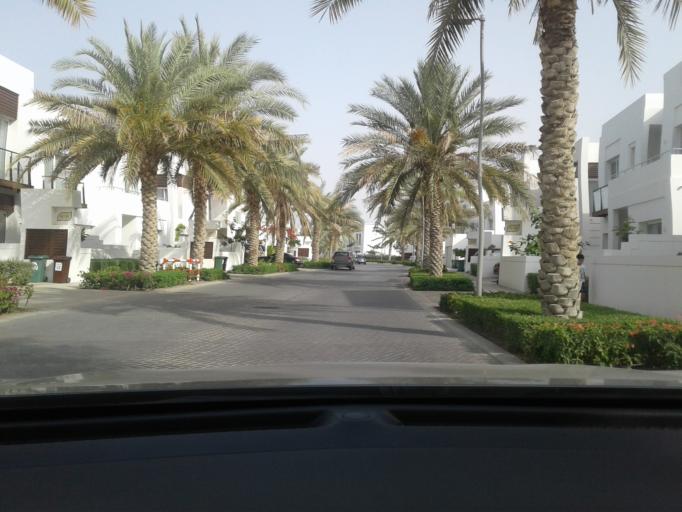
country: OM
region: Muhafazat Masqat
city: As Sib al Jadidah
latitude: 23.6209
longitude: 58.2777
